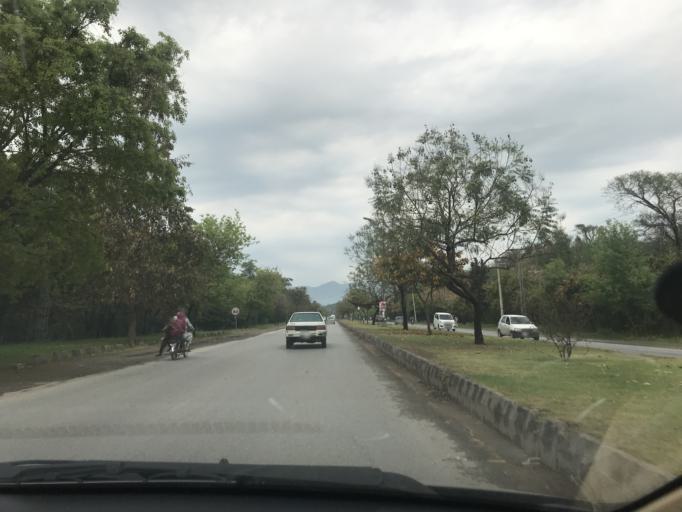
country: PK
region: Islamabad
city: Islamabad
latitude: 33.6794
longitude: 73.1398
